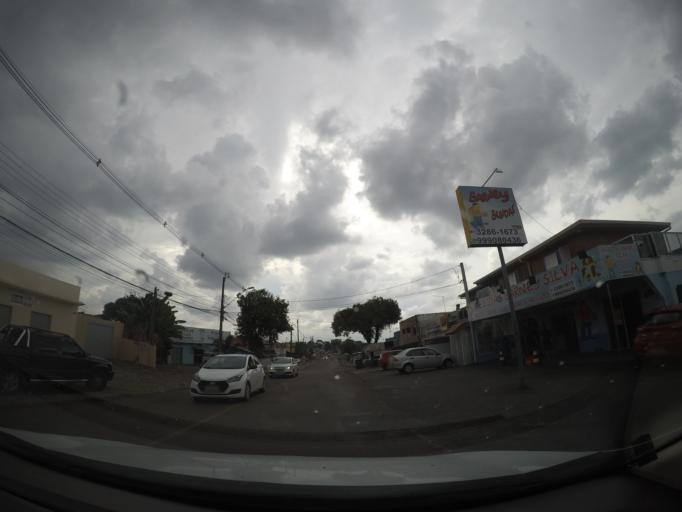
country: BR
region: Parana
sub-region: Sao Jose Dos Pinhais
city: Sao Jose dos Pinhais
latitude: -25.5394
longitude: -49.2417
